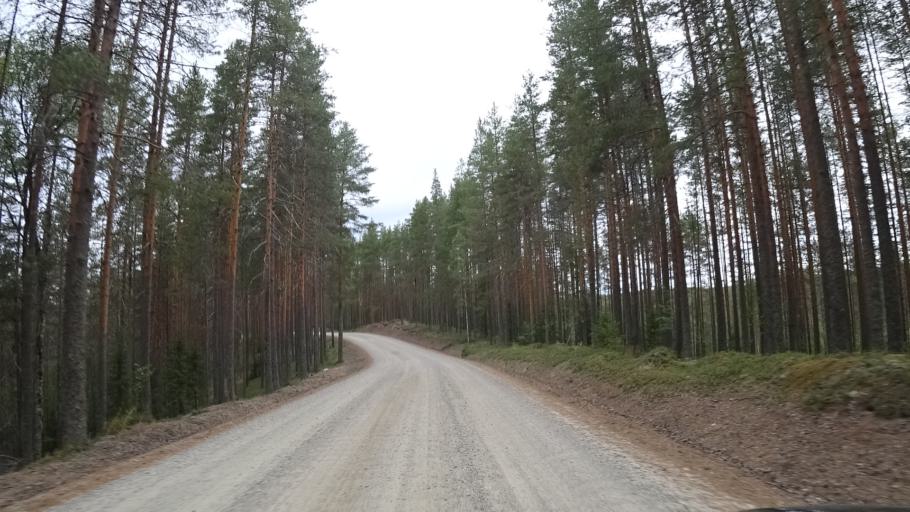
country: FI
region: North Karelia
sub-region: Pielisen Karjala
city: Lieksa
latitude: 63.2448
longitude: 30.3420
